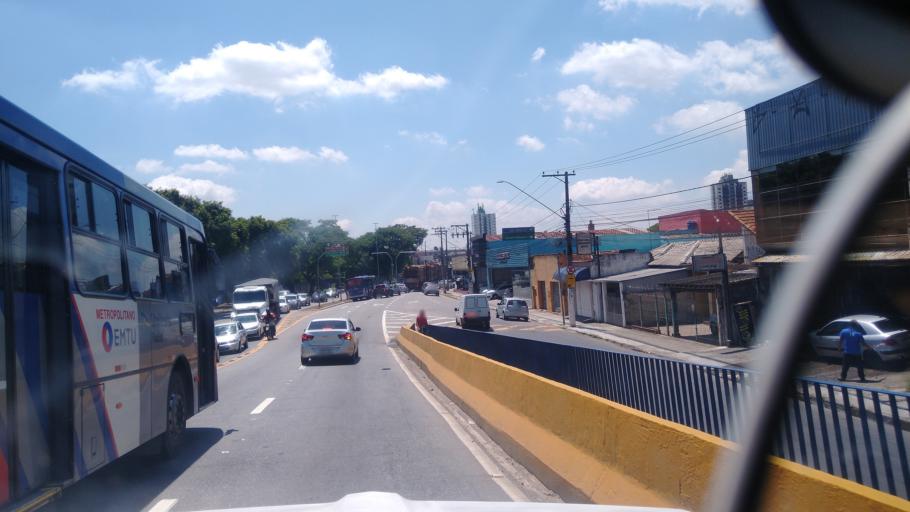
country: BR
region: Sao Paulo
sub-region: Suzano
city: Suzano
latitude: -23.5324
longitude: -46.3137
